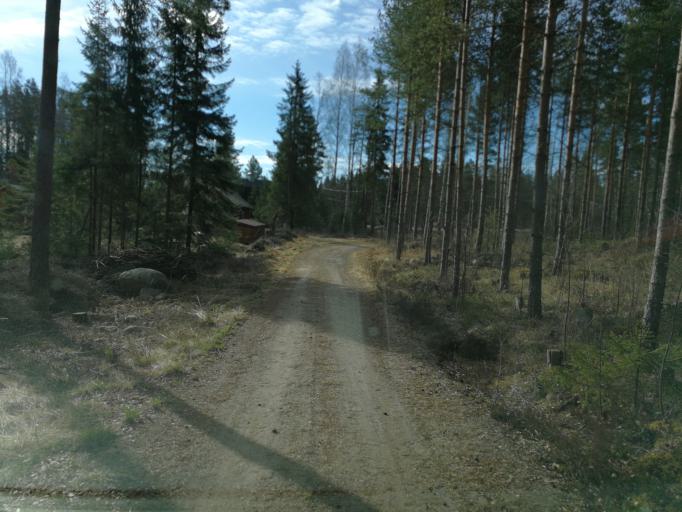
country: FI
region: Uusimaa
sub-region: Helsinki
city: Karjalohja
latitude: 60.2112
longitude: 23.6665
